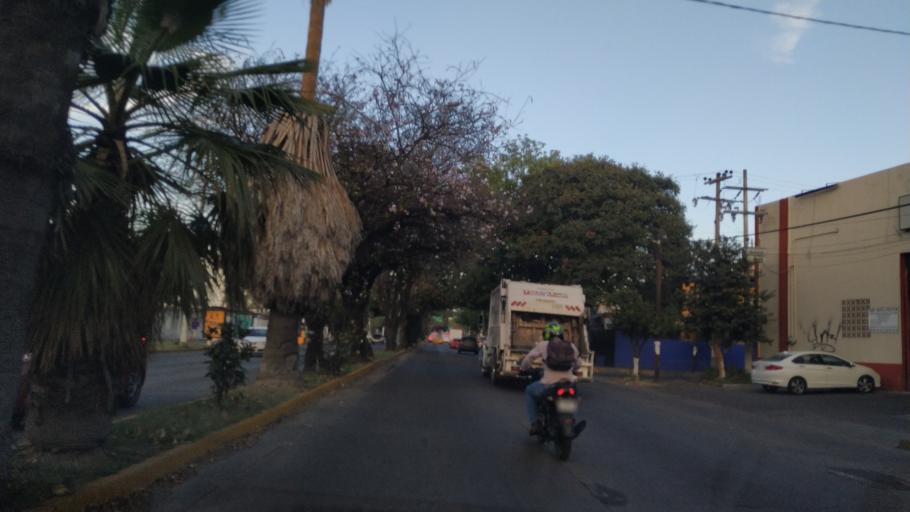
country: MX
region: Jalisco
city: Tlaquepaque
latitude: 20.6548
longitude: -103.3220
